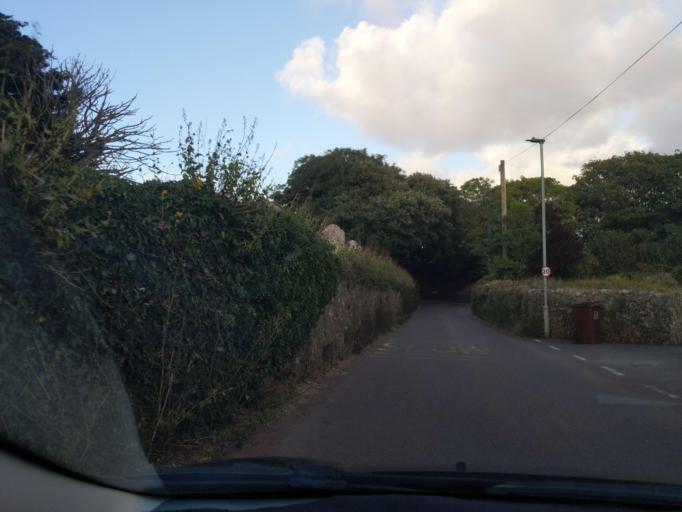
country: GB
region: England
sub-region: Devon
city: Salcombe
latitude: 50.2438
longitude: -3.8152
